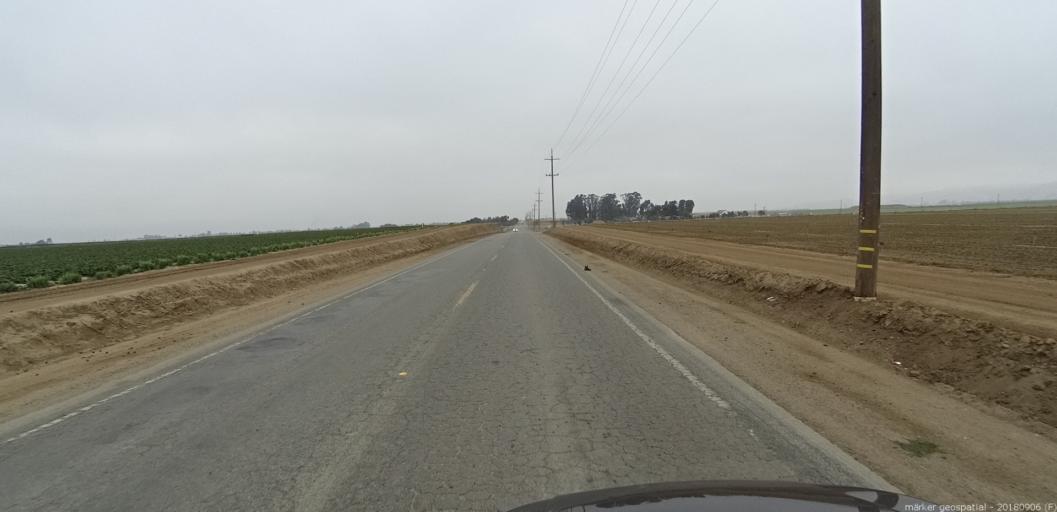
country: US
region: California
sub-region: Monterey County
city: Salinas
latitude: 36.6576
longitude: -121.5876
